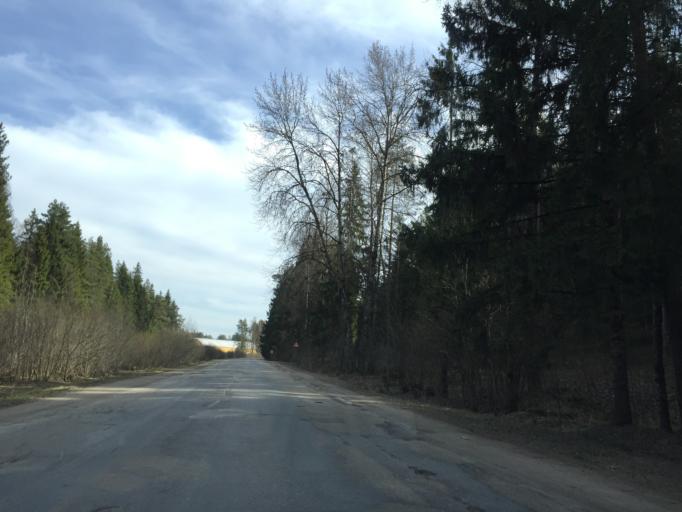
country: LV
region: Ogre
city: Ogre
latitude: 56.8286
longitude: 24.5936
